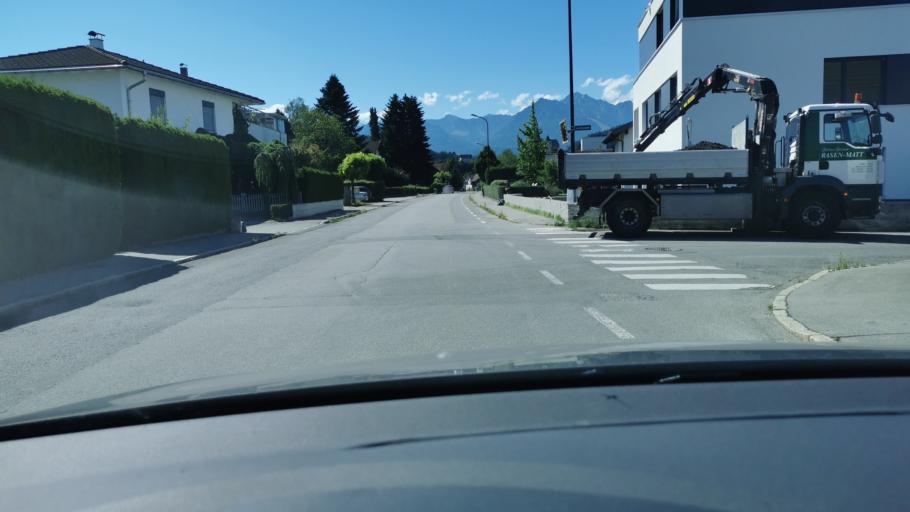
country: AT
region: Vorarlberg
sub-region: Politischer Bezirk Feldkirch
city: Rankweil
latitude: 47.2780
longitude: 9.6449
